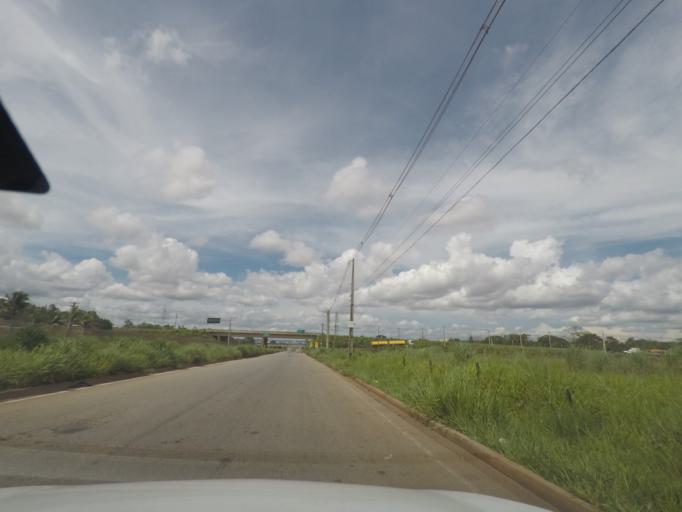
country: BR
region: Goias
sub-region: Goiania
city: Goiania
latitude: -16.7135
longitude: -49.3585
